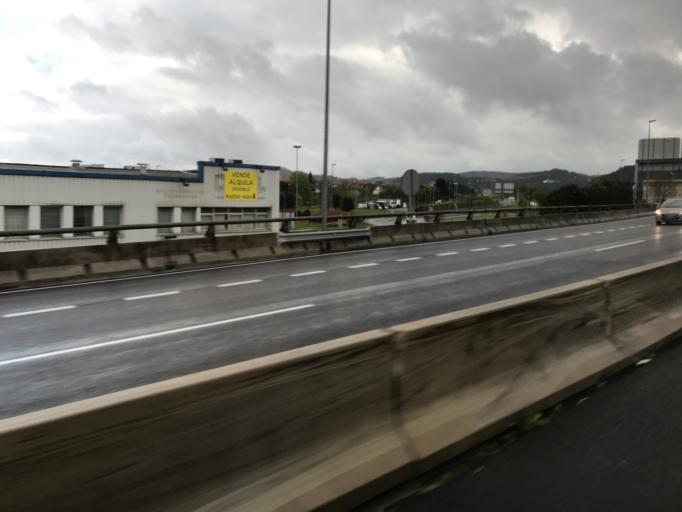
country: ES
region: Basque Country
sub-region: Bizkaia
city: Zamudio
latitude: 43.2883
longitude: -2.8808
